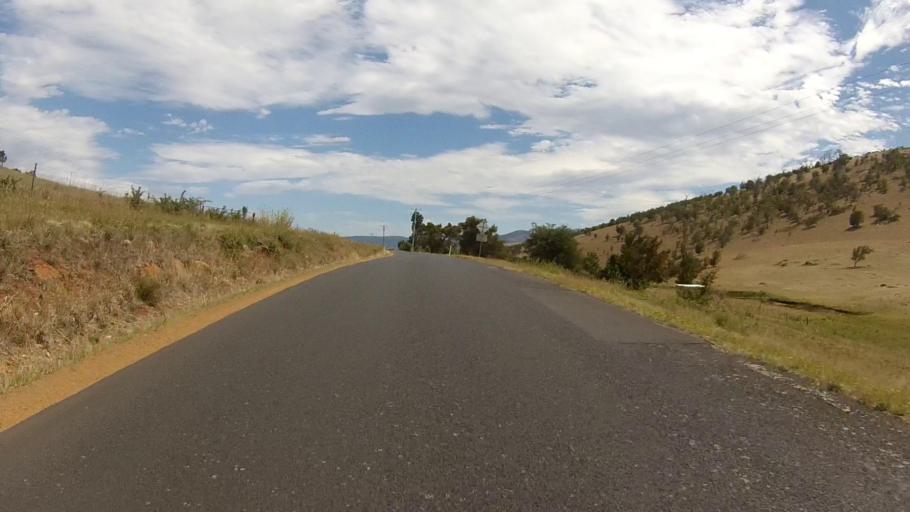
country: AU
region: Tasmania
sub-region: Brighton
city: Old Beach
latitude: -42.7032
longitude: 147.3104
